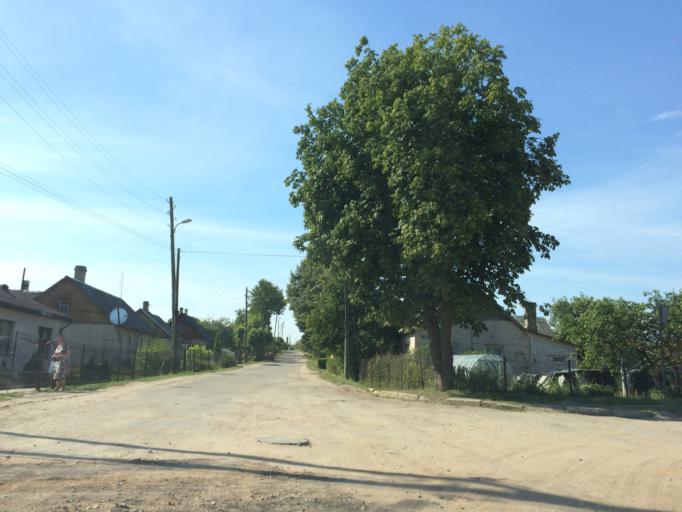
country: LV
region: Rezekne
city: Rezekne
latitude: 56.5145
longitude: 27.3486
